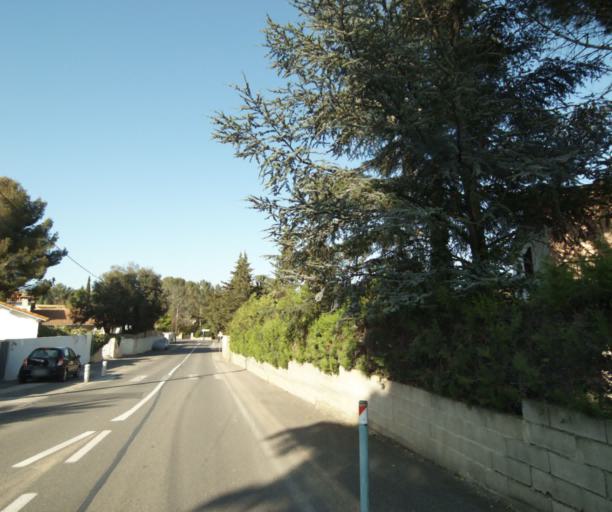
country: FR
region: Languedoc-Roussillon
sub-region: Departement de l'Herault
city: Castelnau-le-Lez
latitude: 43.6422
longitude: 3.9053
